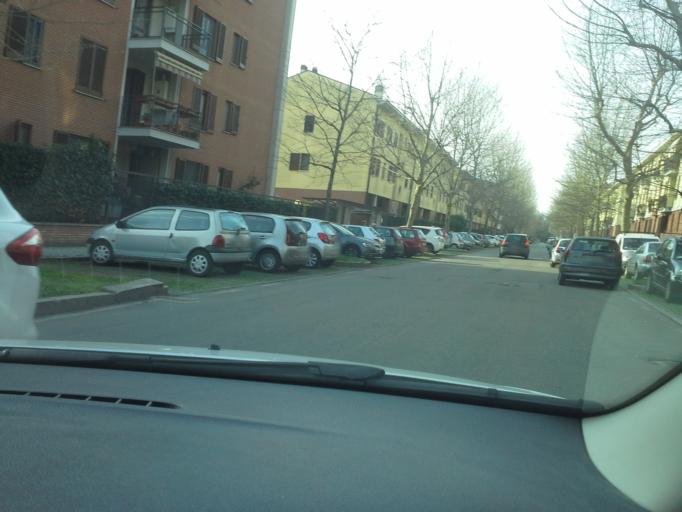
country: IT
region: Lombardy
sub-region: Citta metropolitana di Milano
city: Cesano Boscone
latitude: 45.4507
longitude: 9.0681
